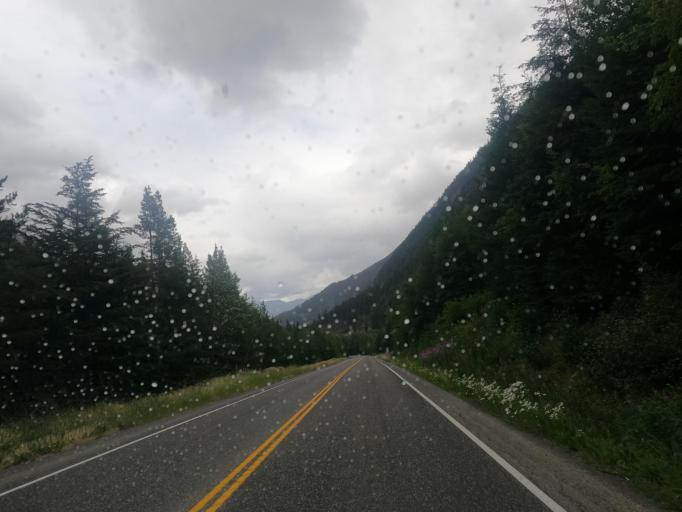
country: CA
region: British Columbia
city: Lillooet
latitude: 50.4957
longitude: -122.1897
